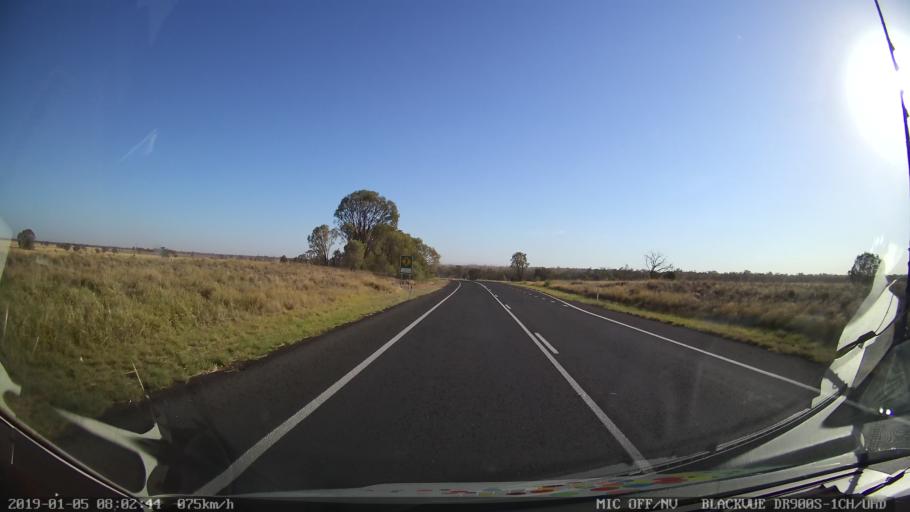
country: AU
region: New South Wales
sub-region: Gilgandra
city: Gilgandra
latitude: -31.6728
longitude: 148.7139
